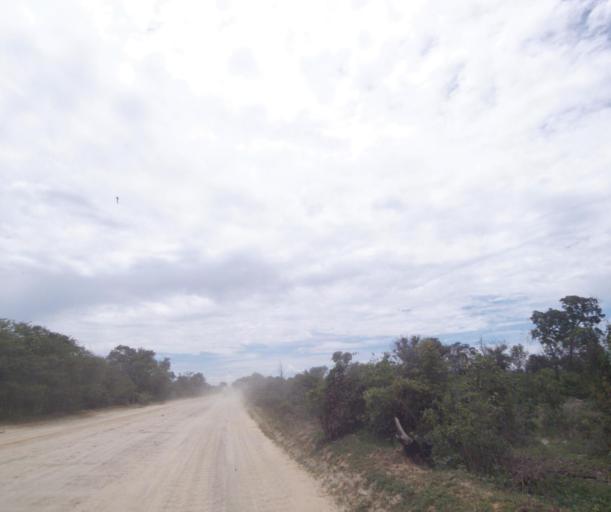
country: BR
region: Bahia
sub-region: Carinhanha
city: Carinhanha
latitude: -14.2172
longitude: -43.8873
